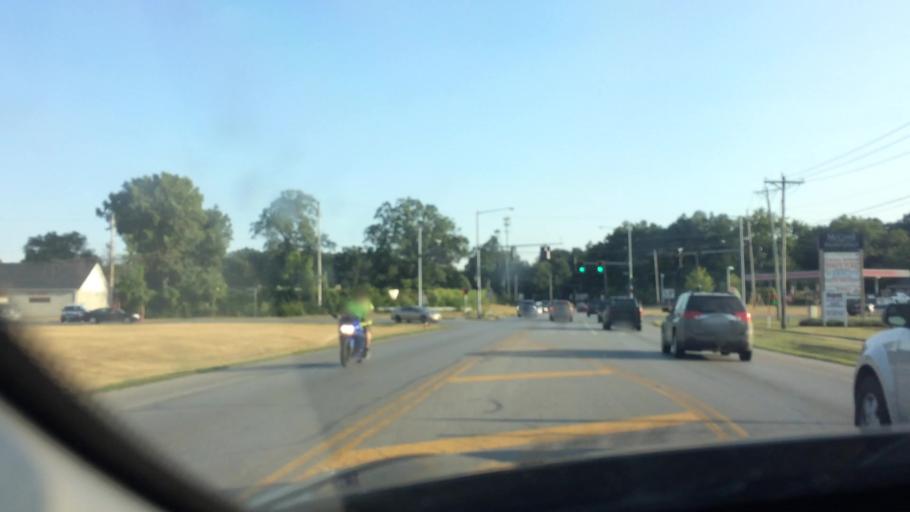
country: US
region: Ohio
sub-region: Lucas County
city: Holland
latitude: 41.6548
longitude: -83.7026
